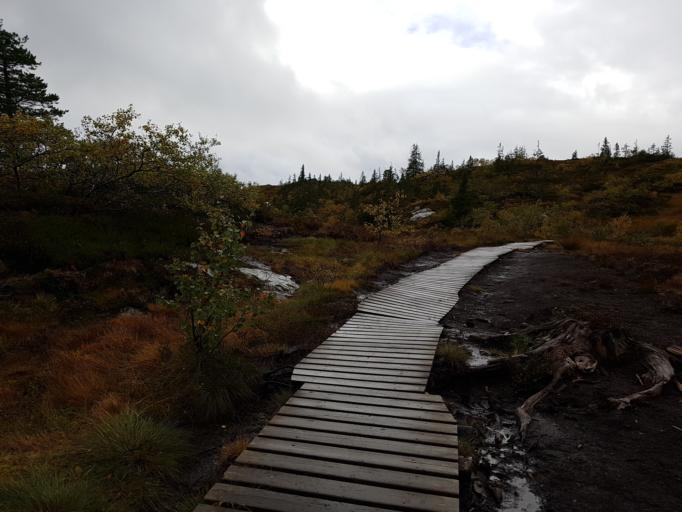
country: NO
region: Sor-Trondelag
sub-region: Melhus
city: Melhus
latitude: 63.4096
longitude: 10.2079
